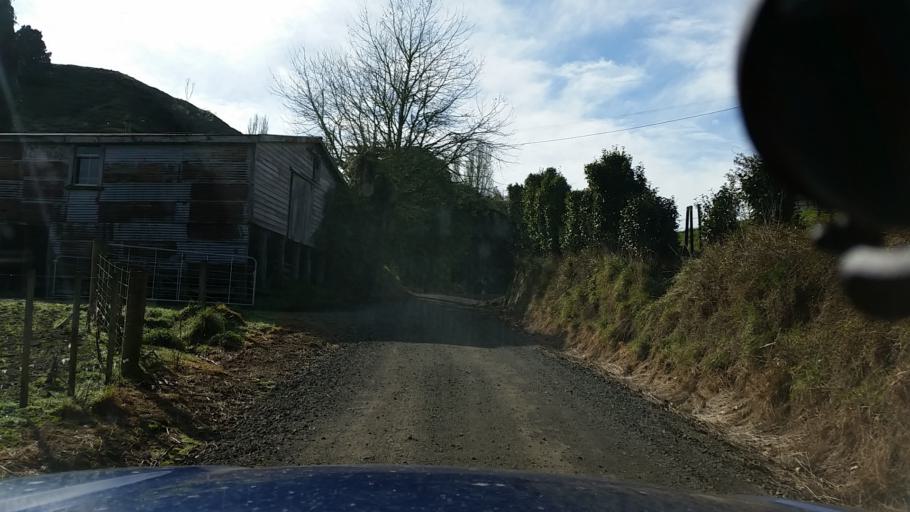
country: NZ
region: Taranaki
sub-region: New Plymouth District
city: Waitara
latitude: -39.0342
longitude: 174.7836
